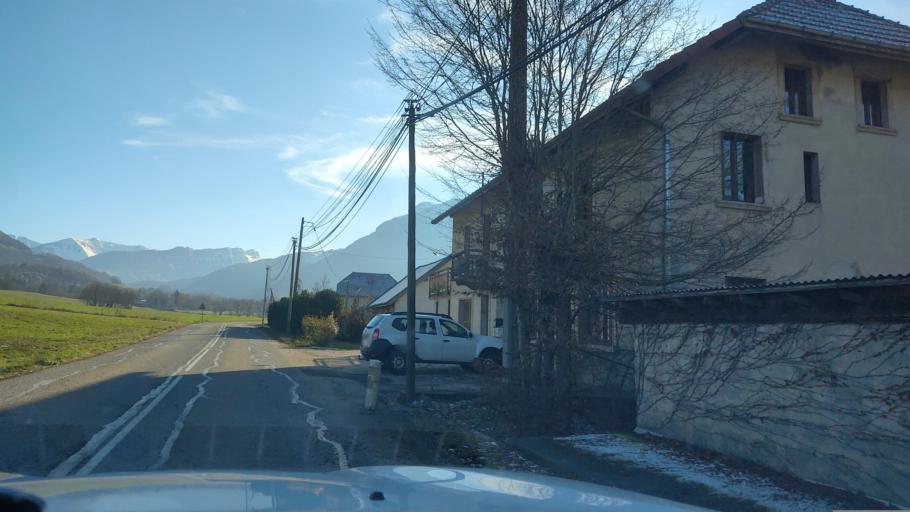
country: FR
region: Rhone-Alpes
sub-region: Departement de la Haute-Savoie
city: Gruffy
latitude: 45.7116
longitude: 6.1126
